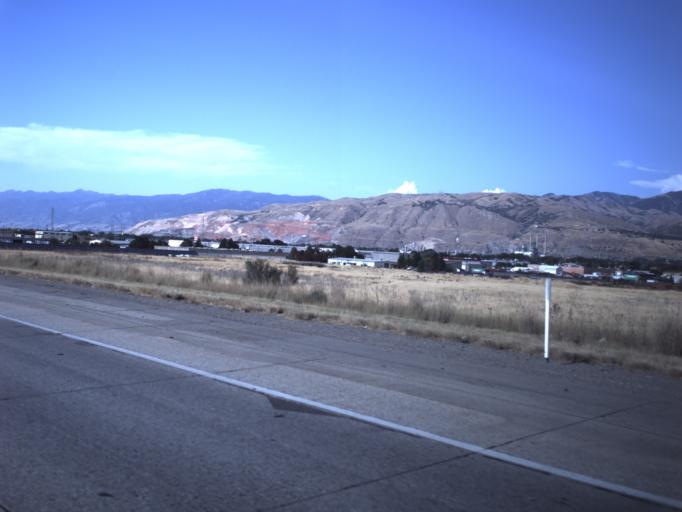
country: US
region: Utah
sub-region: Salt Lake County
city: Salt Lake City
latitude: 40.7530
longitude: -111.9484
